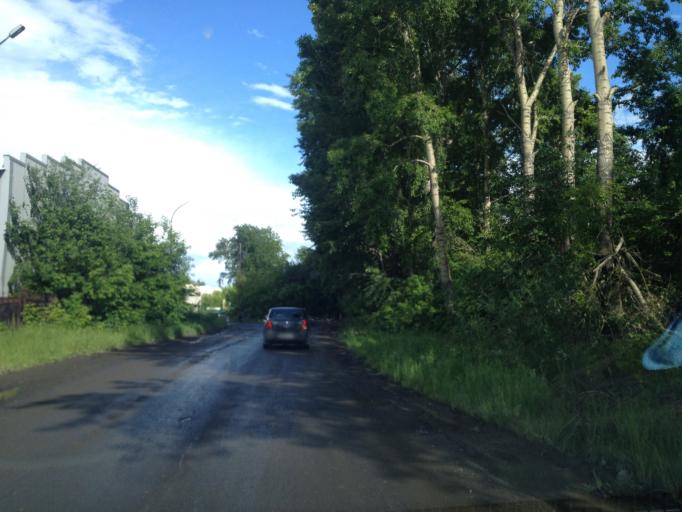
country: RU
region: Sverdlovsk
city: Yekaterinburg
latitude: 56.8171
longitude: 60.6781
